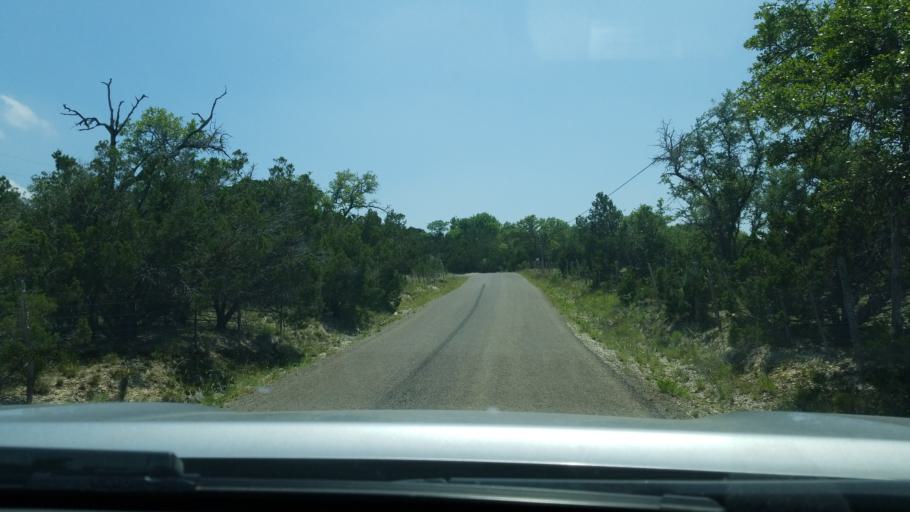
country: US
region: Texas
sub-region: Blanco County
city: Blanco
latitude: 30.0823
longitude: -98.4009
